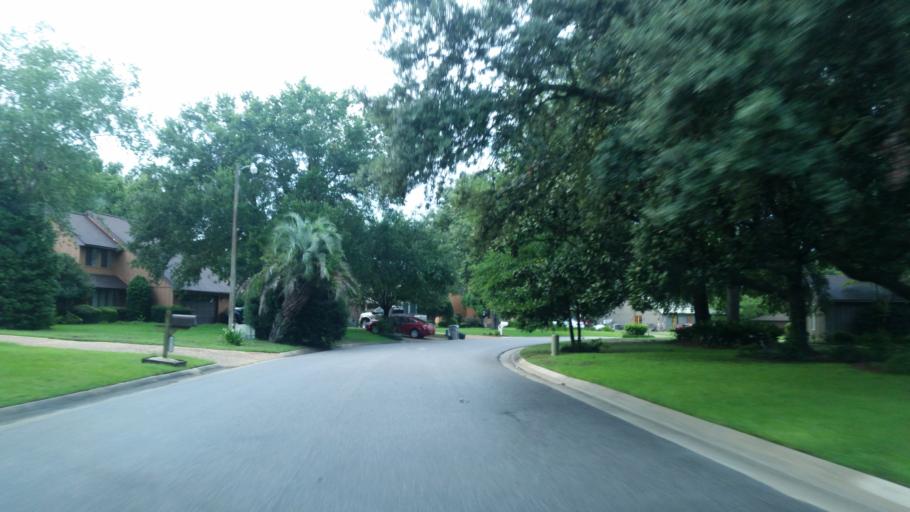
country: US
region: Florida
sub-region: Escambia County
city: Ferry Pass
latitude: 30.5019
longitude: -87.1669
